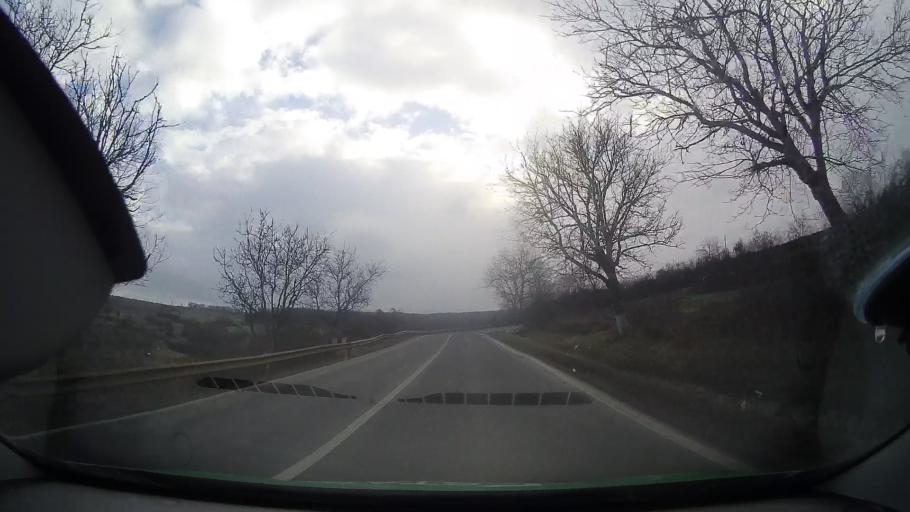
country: RO
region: Mures
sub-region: Municipiul Tarnaveni
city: Tarnaveni
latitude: 46.3593
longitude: 24.2714
